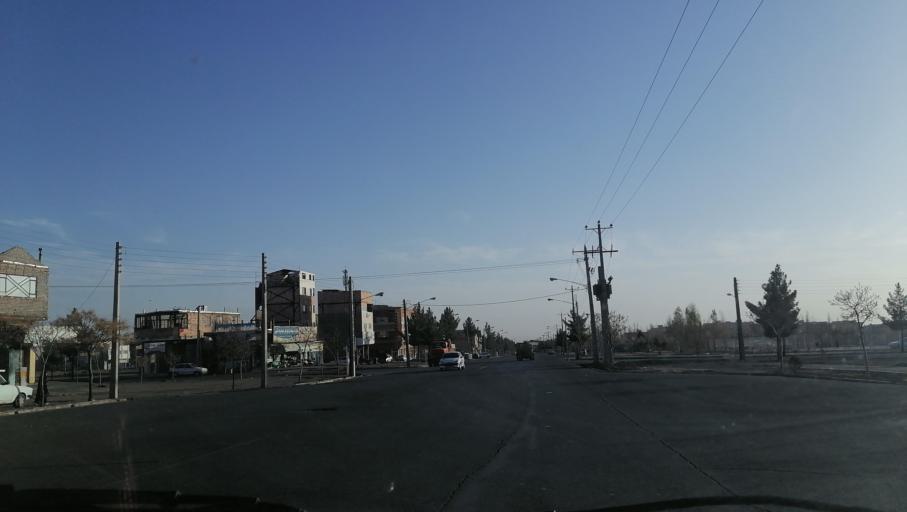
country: IR
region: Razavi Khorasan
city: Sabzevar
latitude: 36.2834
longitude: 57.6750
